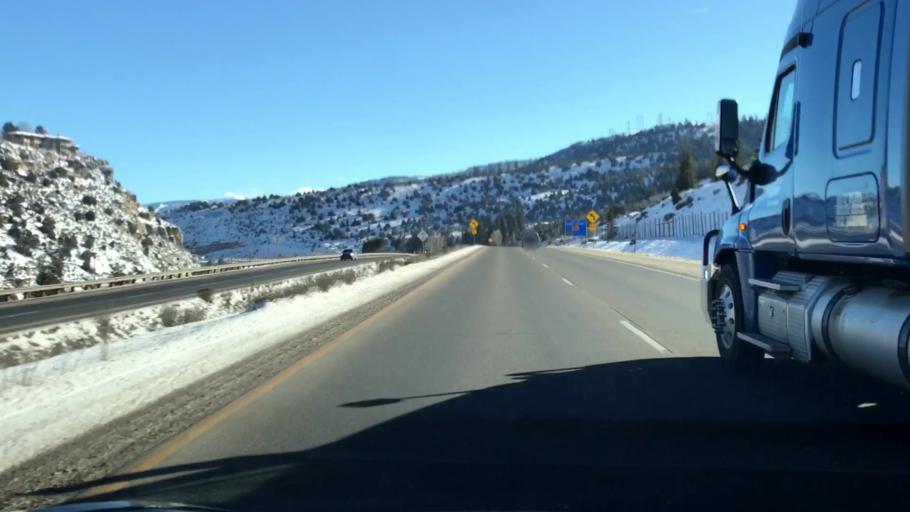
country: US
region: Colorado
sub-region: Eagle County
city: Edwards
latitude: 39.7063
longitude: -106.6912
